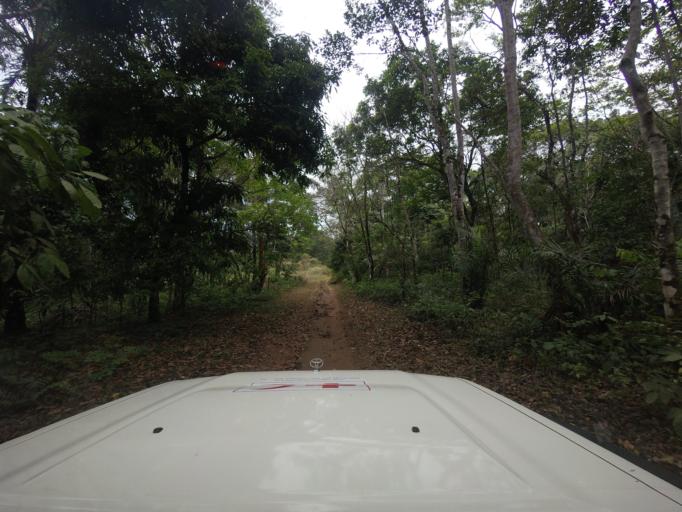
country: SL
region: Eastern Province
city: Buedu
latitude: 8.2168
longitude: -10.2939
